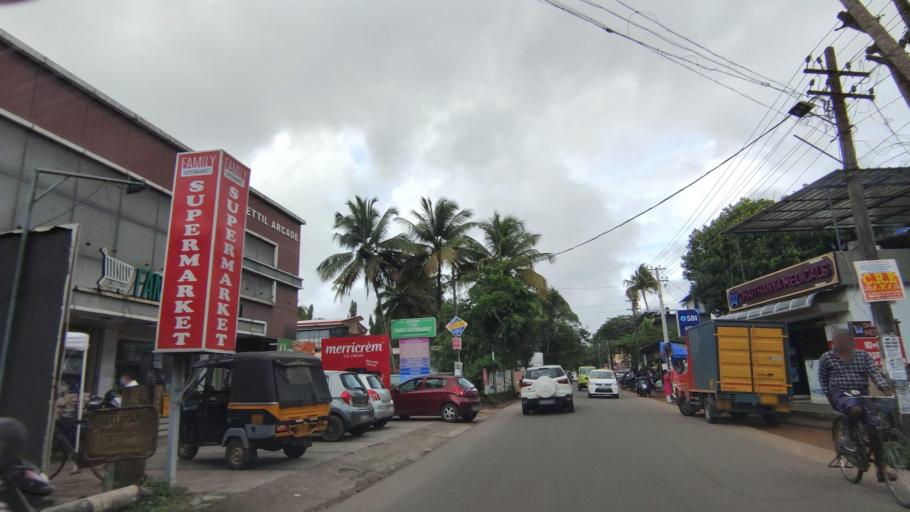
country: IN
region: Kerala
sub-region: Alappuzha
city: Shertallai
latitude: 9.6061
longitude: 76.3599
